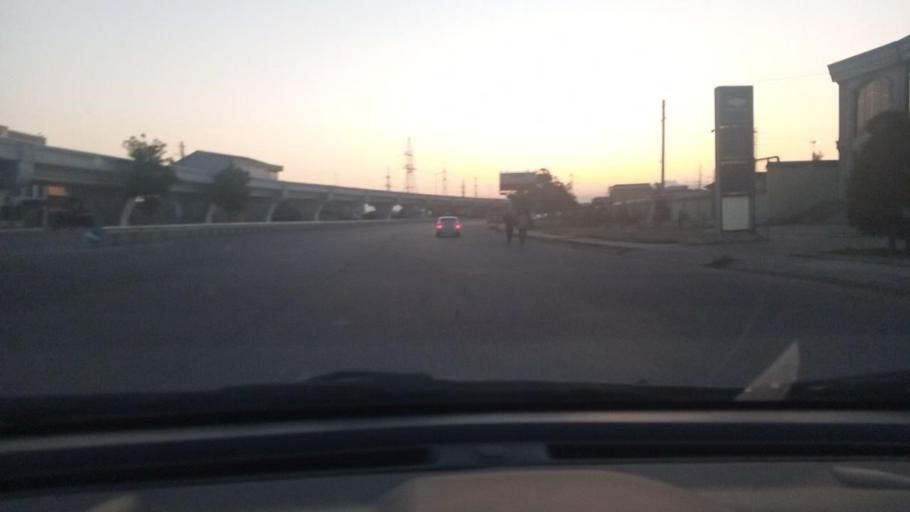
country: UZ
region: Toshkent Shahri
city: Bektemir
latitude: 41.2429
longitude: 69.3375
